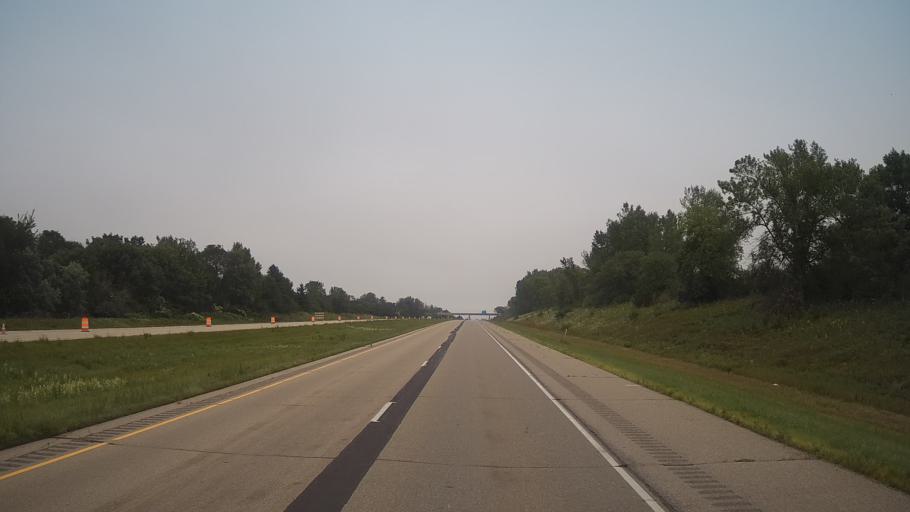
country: US
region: Minnesota
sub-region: Olmsted County
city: Stewartville
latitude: 43.8568
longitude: -92.5291
